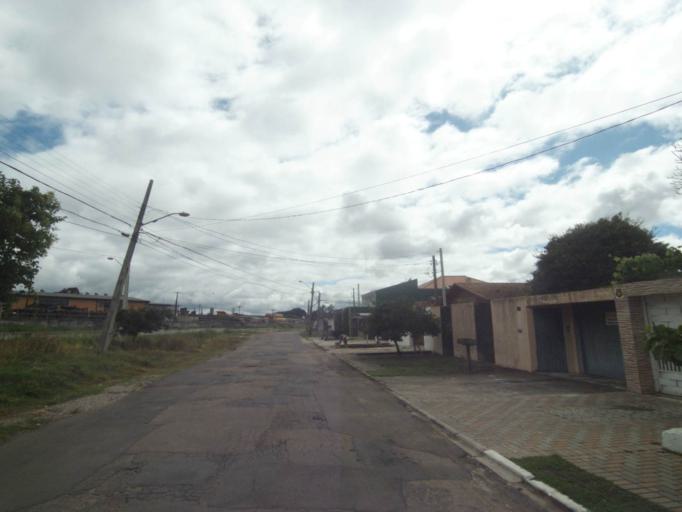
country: BR
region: Parana
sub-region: Curitiba
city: Curitiba
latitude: -25.4749
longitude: -49.2655
